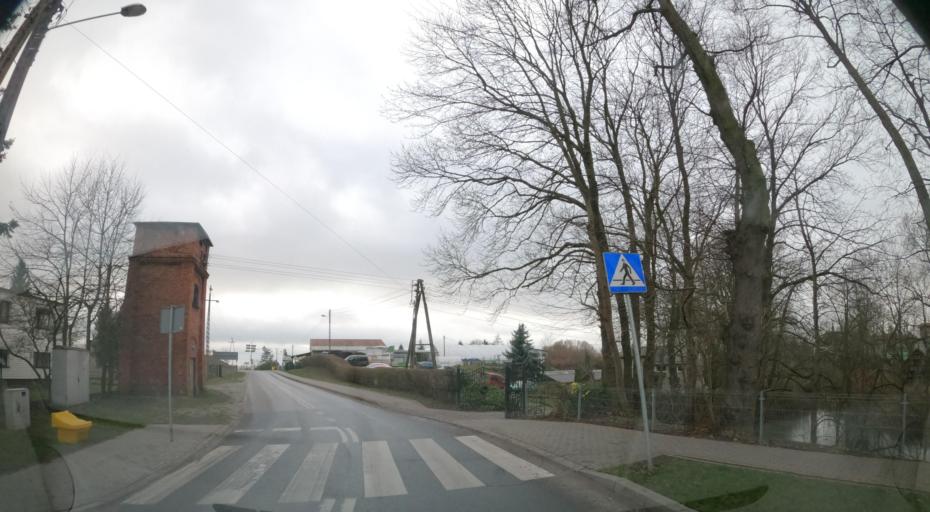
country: PL
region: Greater Poland Voivodeship
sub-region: Powiat pilski
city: Lobzenica
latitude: 53.2595
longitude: 17.2612
